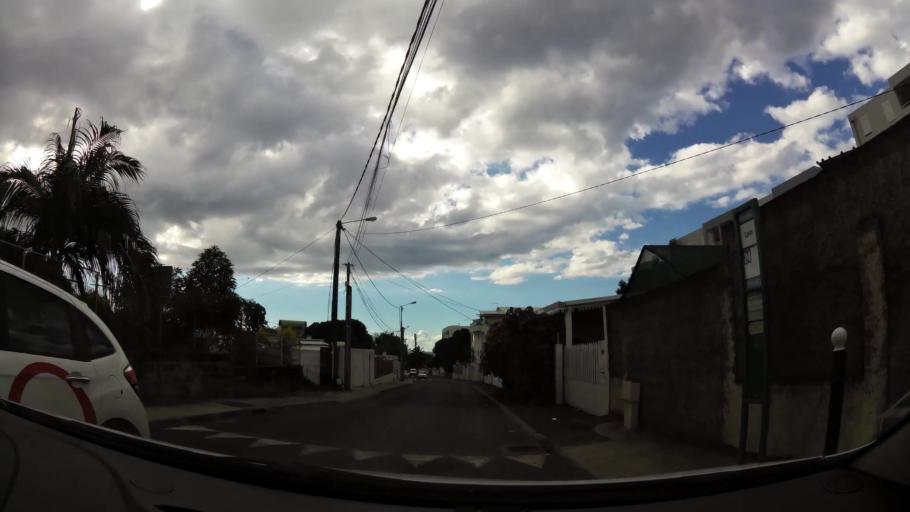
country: RE
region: Reunion
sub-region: Reunion
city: Saint-Denis
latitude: -20.8934
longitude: 55.4740
